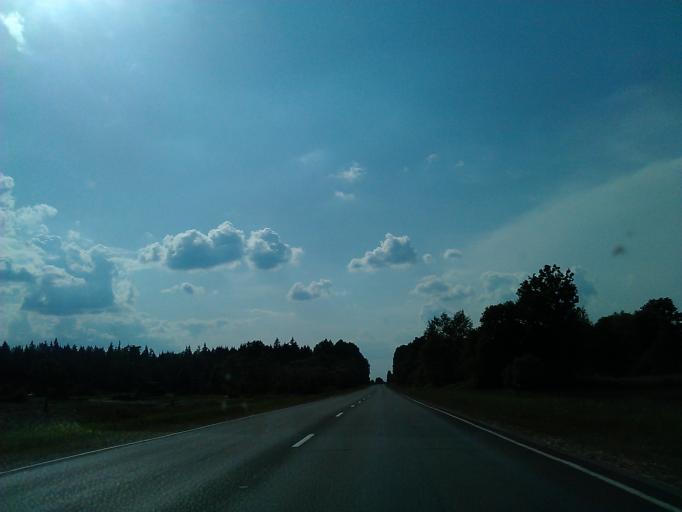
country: LV
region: Skrunda
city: Skrunda
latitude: 56.6789
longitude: 22.1370
